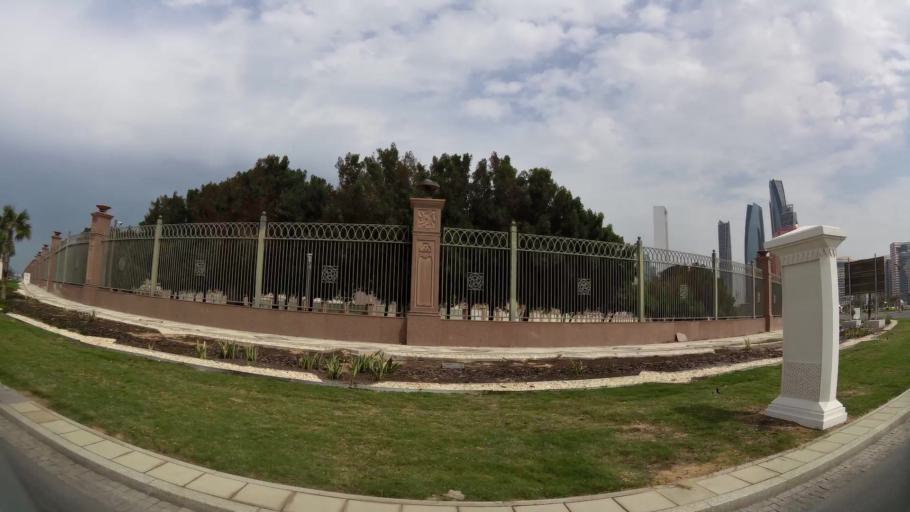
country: AE
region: Abu Dhabi
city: Abu Dhabi
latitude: 24.4573
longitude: 54.3113
